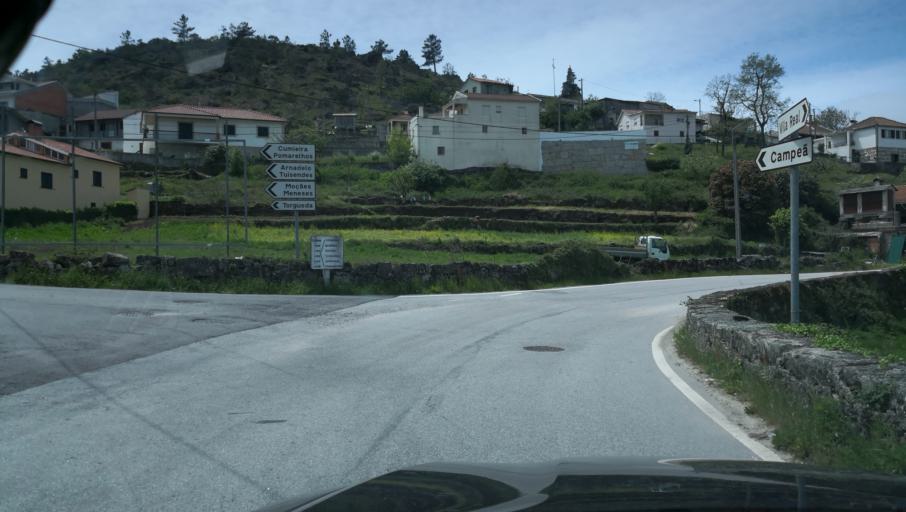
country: PT
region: Vila Real
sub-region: Santa Marta de Penaguiao
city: Santa Marta de Penaguiao
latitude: 41.2816
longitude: -7.8149
